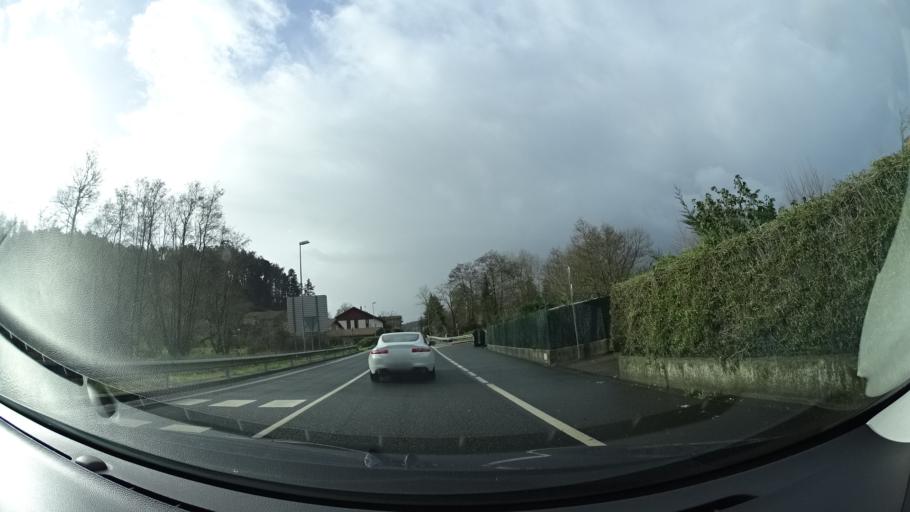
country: ES
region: Basque Country
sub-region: Bizkaia
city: Mungia
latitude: 43.3730
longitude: -2.8029
